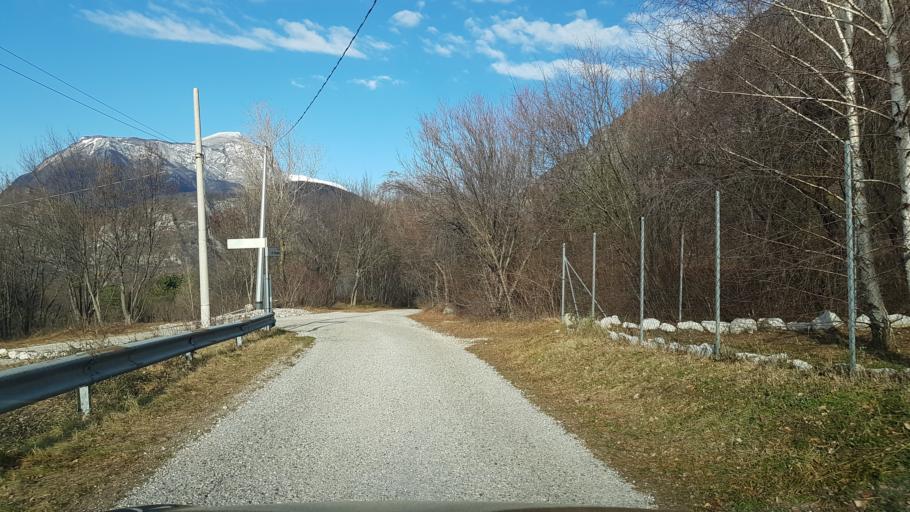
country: IT
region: Friuli Venezia Giulia
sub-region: Provincia di Udine
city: Gemona
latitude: 46.2865
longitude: 13.1443
